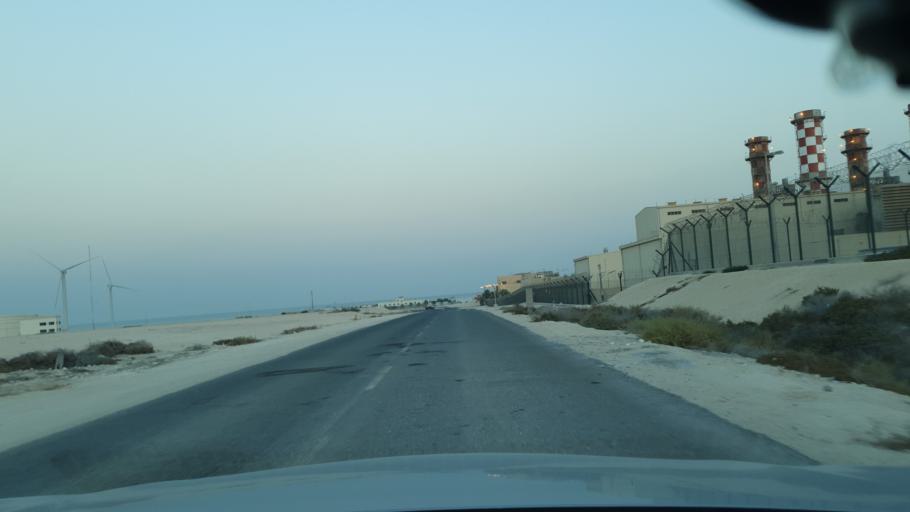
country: BH
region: Central Governorate
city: Dar Kulayb
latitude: 25.9734
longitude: 50.6058
